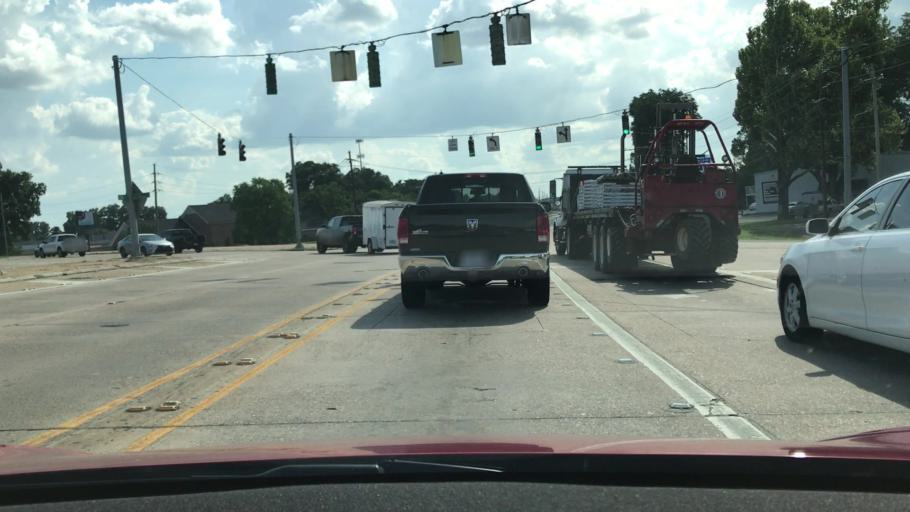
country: US
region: Louisiana
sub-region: Bossier Parish
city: Bossier City
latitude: 32.4461
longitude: -93.7015
